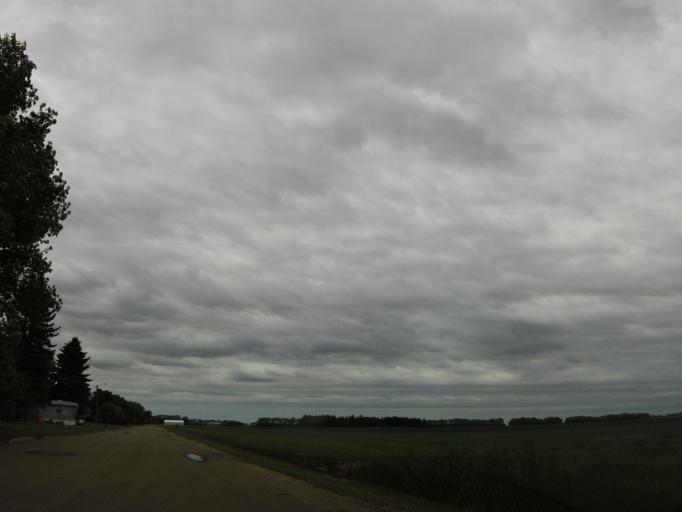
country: US
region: North Dakota
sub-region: Walsh County
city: Grafton
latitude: 48.6161
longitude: -97.4417
